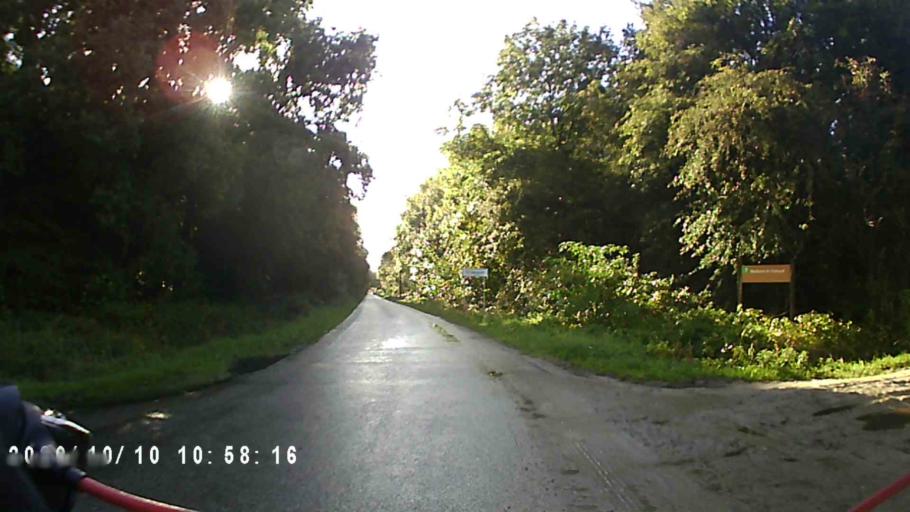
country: NL
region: Friesland
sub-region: Gemeente Achtkarspelen
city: Surhuisterveen
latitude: 53.1454
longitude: 6.2064
